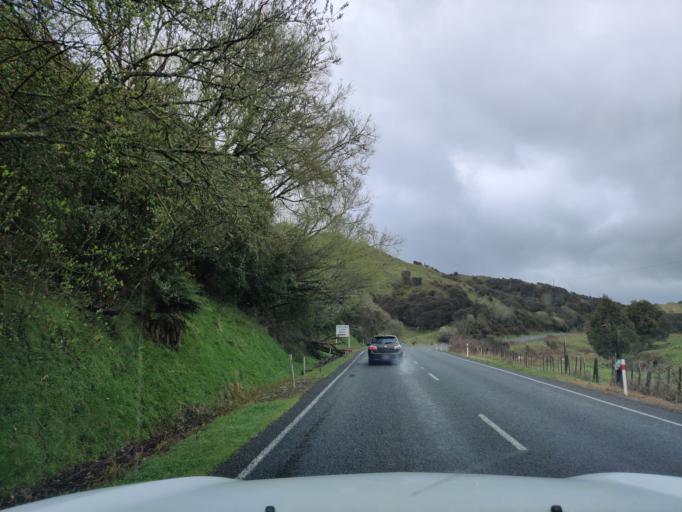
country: NZ
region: Waikato
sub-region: Otorohanga District
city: Otorohanga
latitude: -38.6266
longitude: 175.2126
